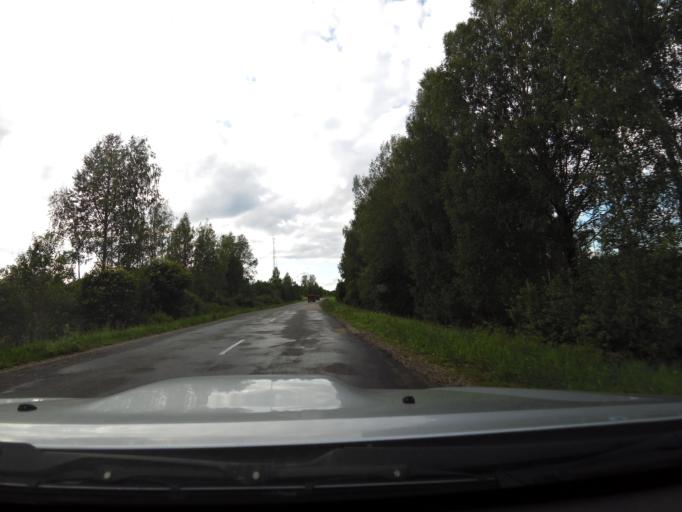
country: LV
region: Akniste
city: Akniste
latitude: 56.0119
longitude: 25.9308
